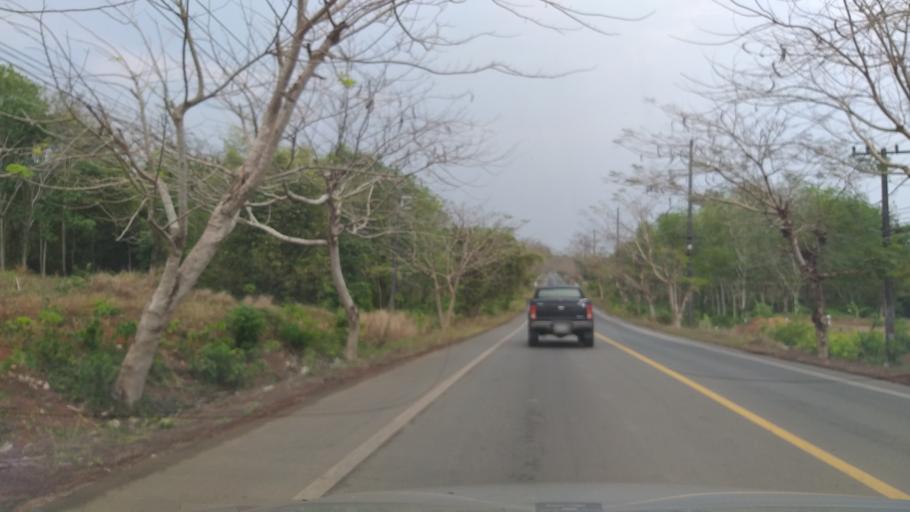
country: TH
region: Trat
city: Khao Saming
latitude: 12.3113
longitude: 102.3519
